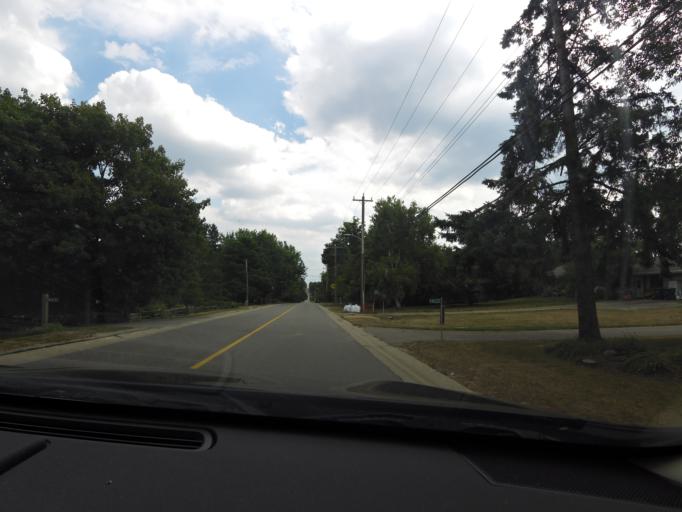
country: CA
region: Ontario
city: Brampton
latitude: 43.7567
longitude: -79.9279
